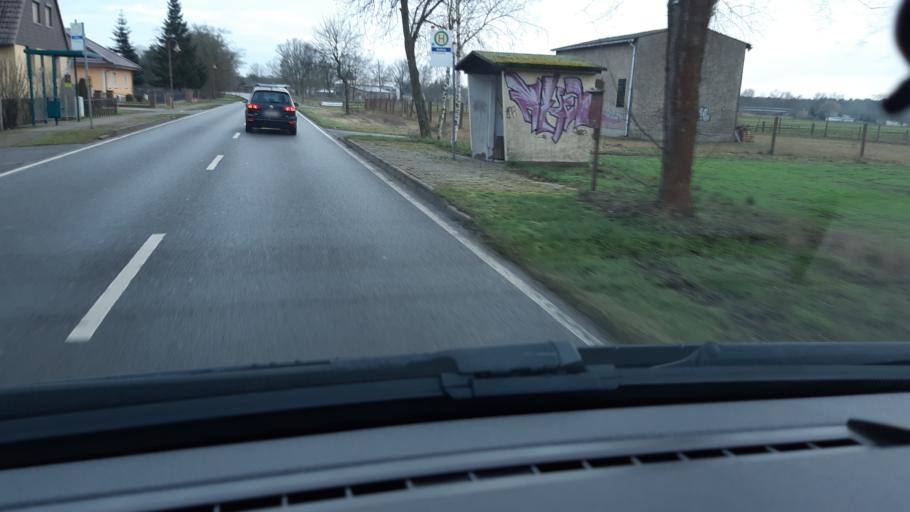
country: DE
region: Brandenburg
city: Zehdenick
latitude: 52.9515
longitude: 13.3816
